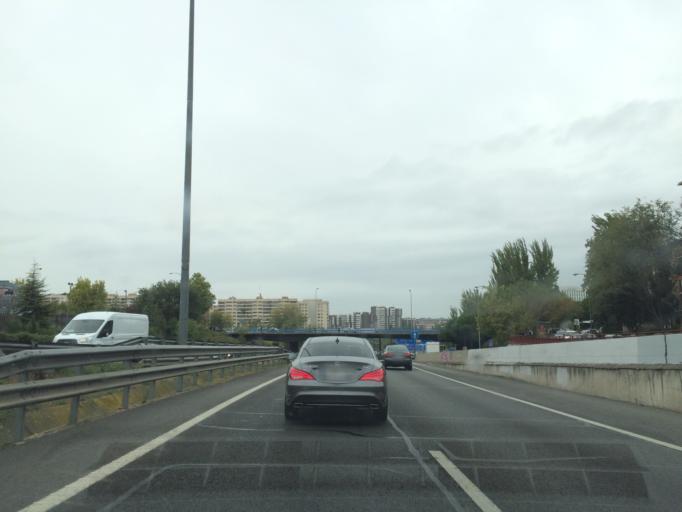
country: ES
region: Madrid
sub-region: Provincia de Madrid
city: Pinar de Chamartin
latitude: 40.4831
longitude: -3.6872
